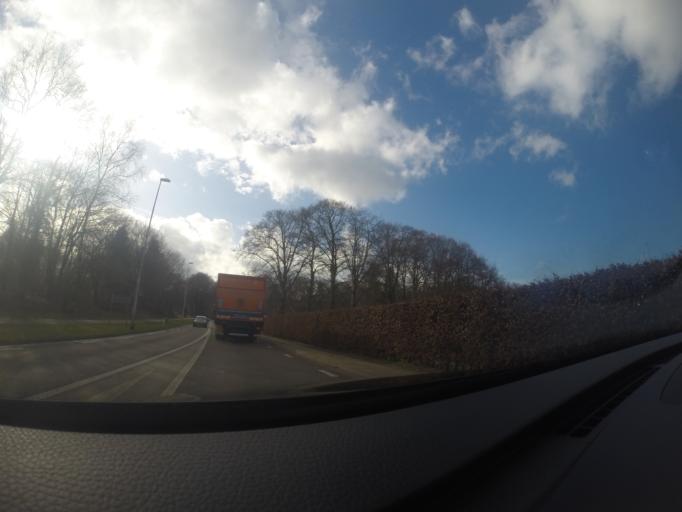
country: NL
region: Gelderland
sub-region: Gemeente Bronckhorst
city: Hengelo
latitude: 52.1065
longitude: 6.3474
